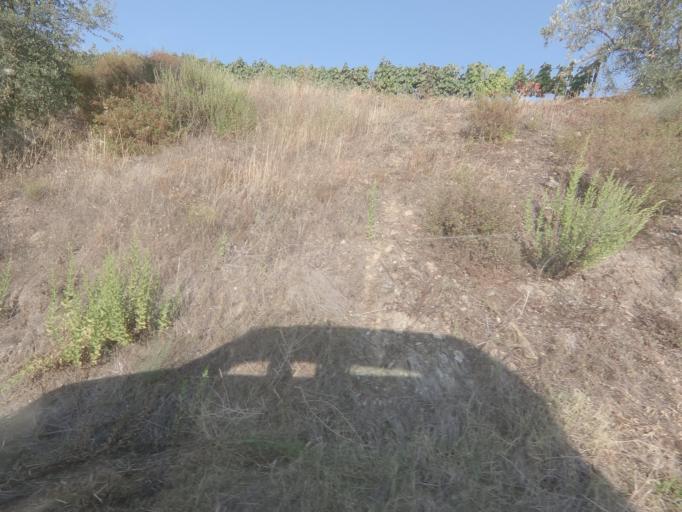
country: PT
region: Vila Real
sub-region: Sabrosa
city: Sabrosa
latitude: 41.2650
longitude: -7.5409
